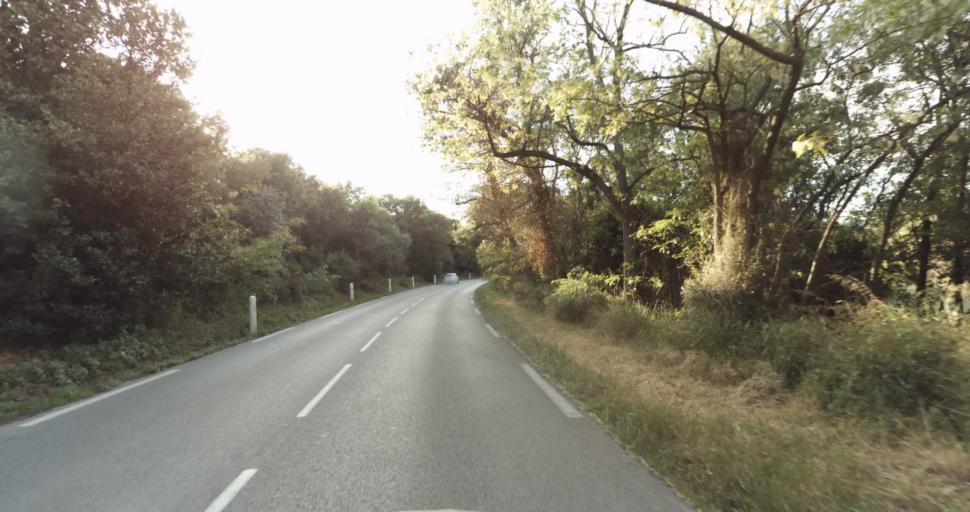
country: FR
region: Provence-Alpes-Cote d'Azur
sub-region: Departement du Var
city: Hyeres
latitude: 43.1343
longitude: 6.1590
